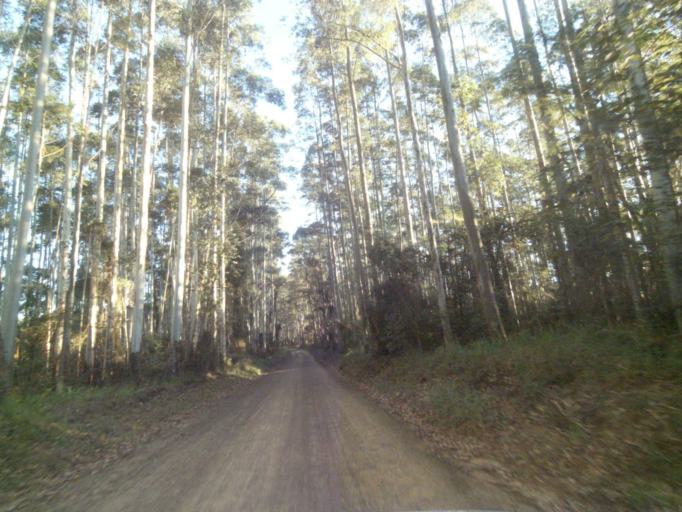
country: BR
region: Parana
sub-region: Telemaco Borba
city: Telemaco Borba
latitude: -24.5077
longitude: -50.6015
